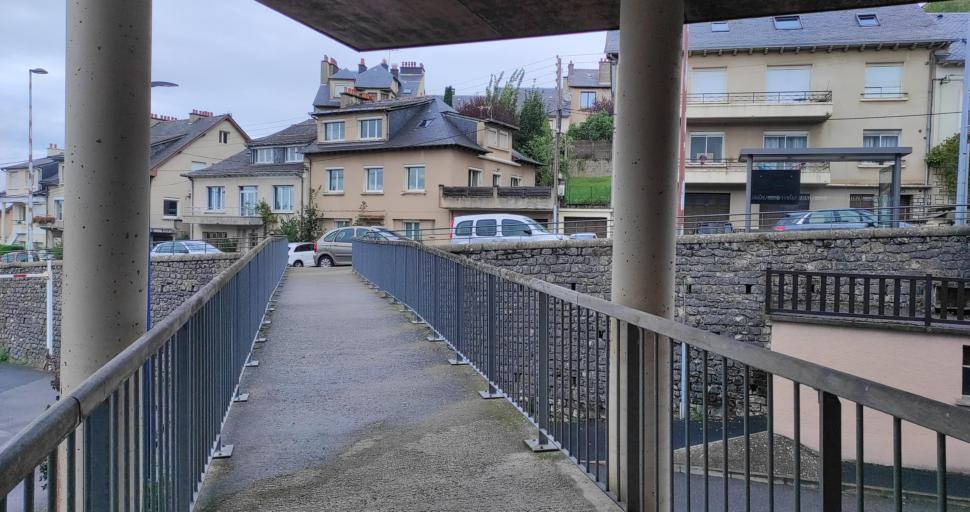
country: FR
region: Midi-Pyrenees
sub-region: Departement de l'Aveyron
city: Rodez
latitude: 44.3545
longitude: 2.5670
